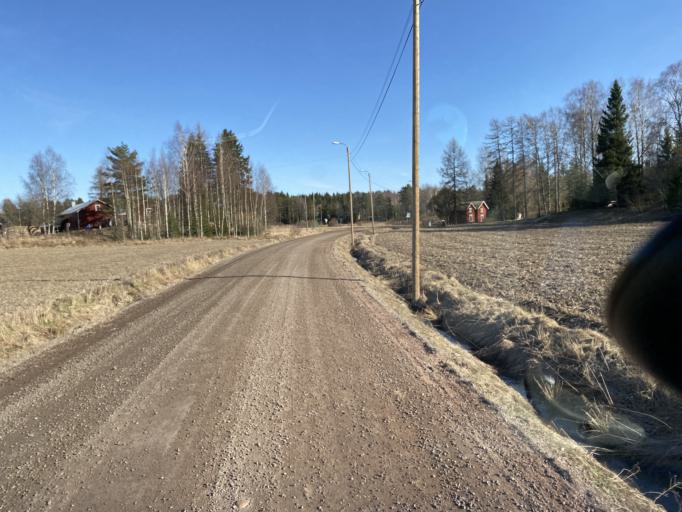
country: FI
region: Satakunta
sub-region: Rauma
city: Lappi
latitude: 61.1397
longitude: 21.9464
